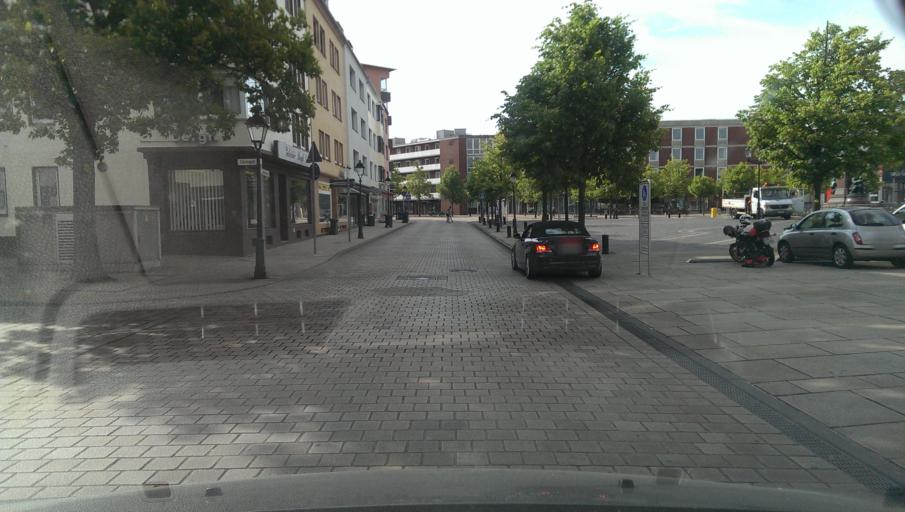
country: DE
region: Bremen
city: Bremerhaven
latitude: 53.5419
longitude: 8.5819
